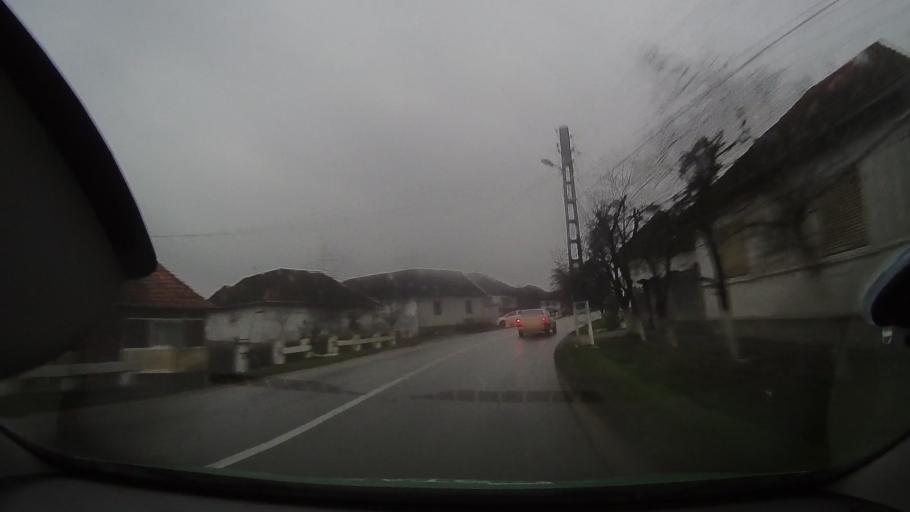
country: RO
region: Arad
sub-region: Comuna Craiova
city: Craiova
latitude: 46.5503
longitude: 21.9605
